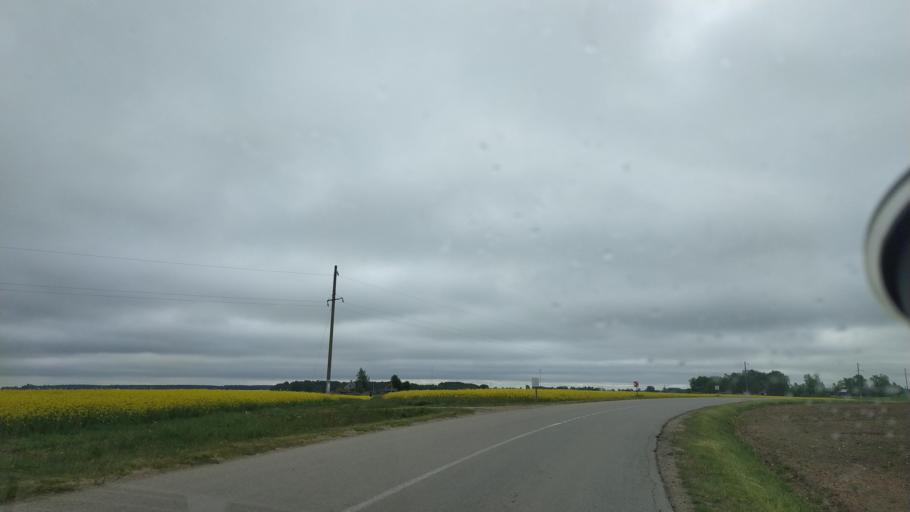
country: LT
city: Vabalninkas
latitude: 55.9922
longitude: 24.7042
